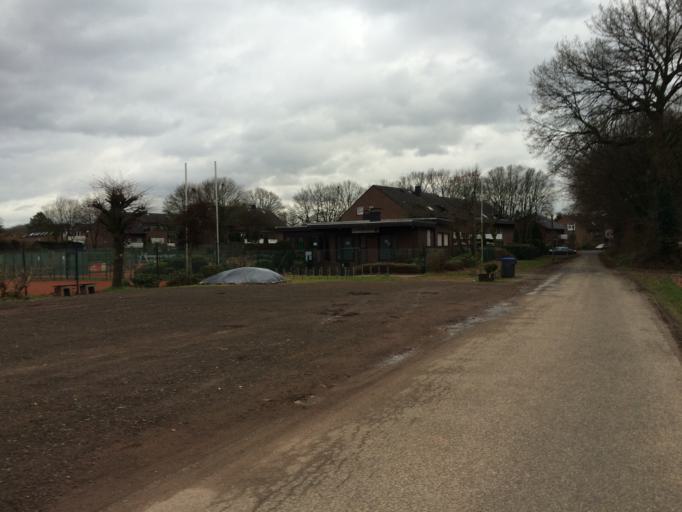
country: DE
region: North Rhine-Westphalia
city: Dorsten
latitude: 51.6758
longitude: 7.0155
